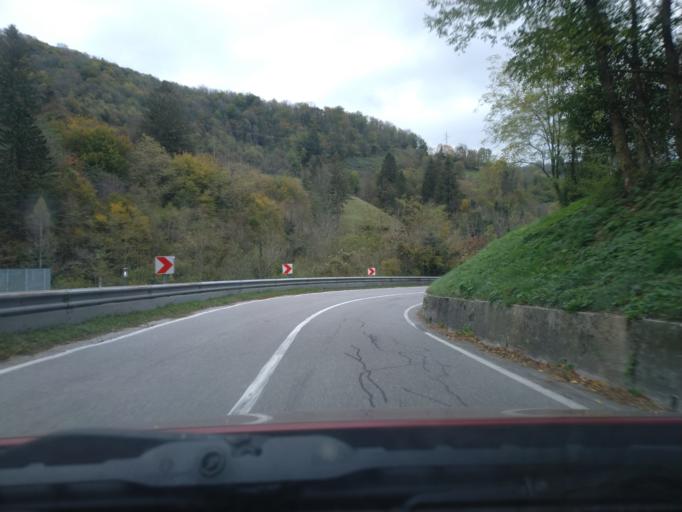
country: SI
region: Tolmin
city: Tolmin
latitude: 46.1459
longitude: 13.7161
